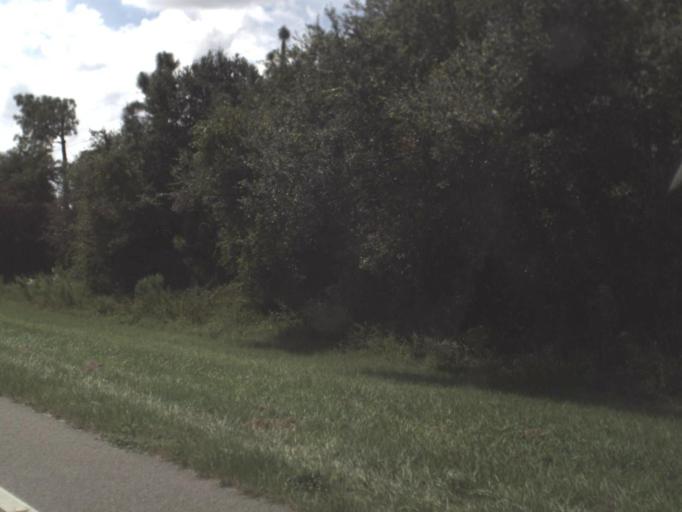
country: US
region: Florida
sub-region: Collier County
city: Immokalee
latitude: 26.3524
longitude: -81.3437
